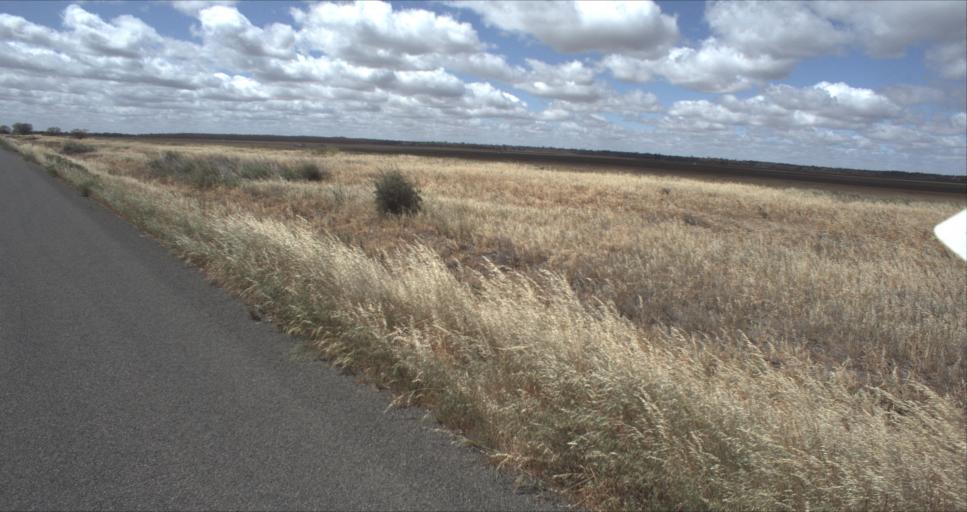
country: AU
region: New South Wales
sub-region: Murrumbidgee Shire
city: Darlington Point
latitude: -34.5768
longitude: 146.1838
